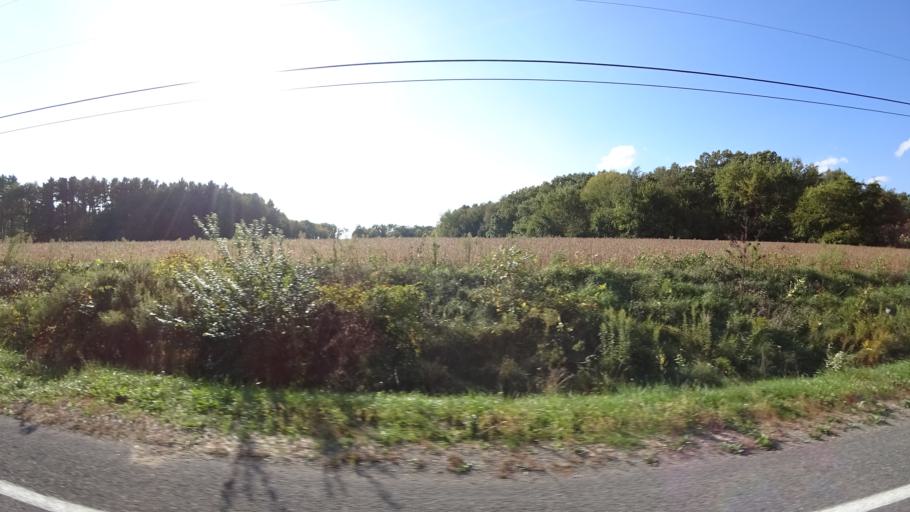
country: US
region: Michigan
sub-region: Saint Joseph County
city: Centreville
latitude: 41.8603
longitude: -85.5066
